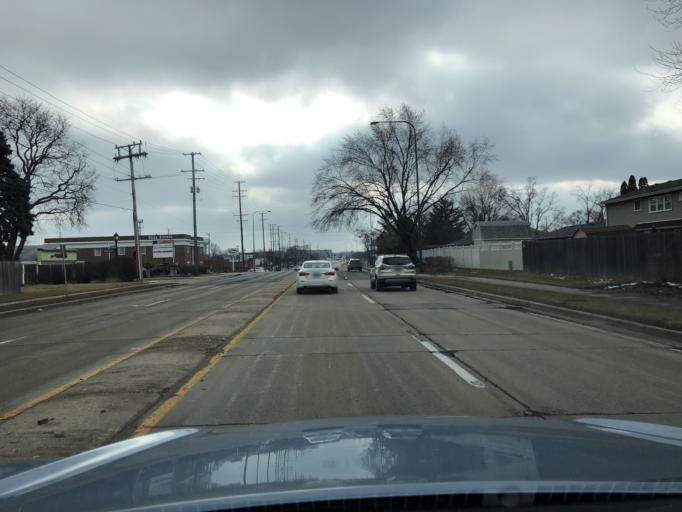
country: US
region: Illinois
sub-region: DuPage County
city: Itasca
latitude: 41.9953
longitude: -88.0033
